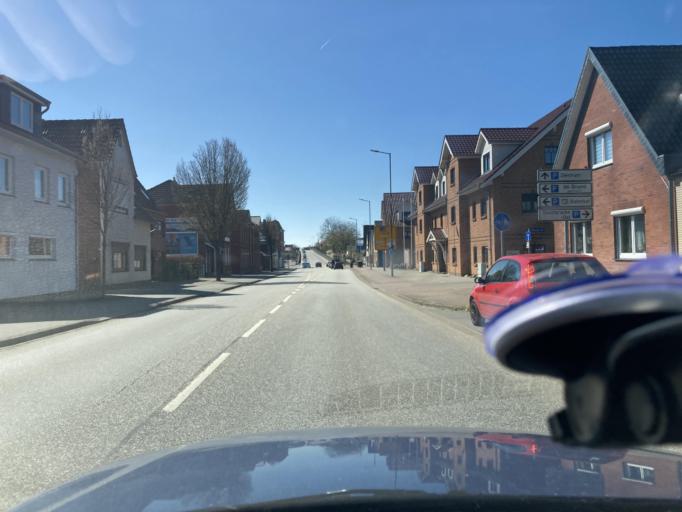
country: DE
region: Schleswig-Holstein
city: Heide
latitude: 54.1965
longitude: 9.1074
